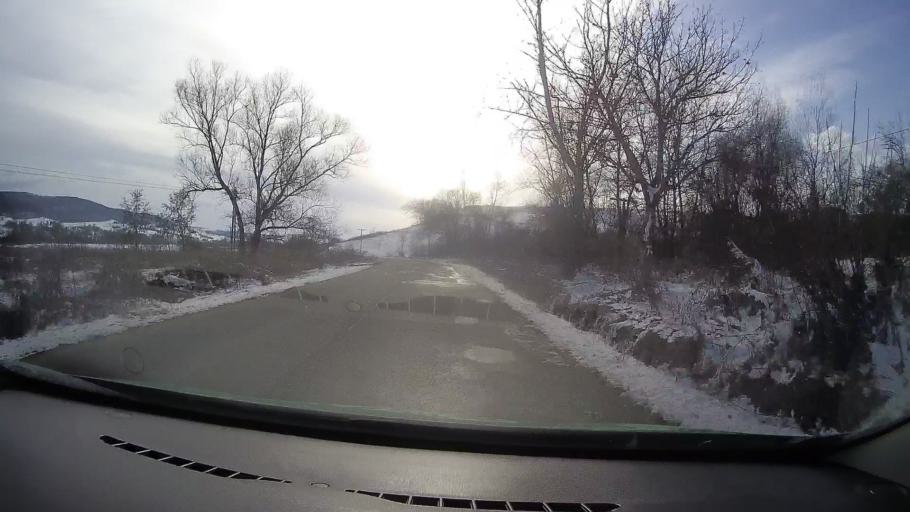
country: RO
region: Sibiu
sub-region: Comuna Iacobeni
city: Iacobeni
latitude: 46.0341
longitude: 24.7182
